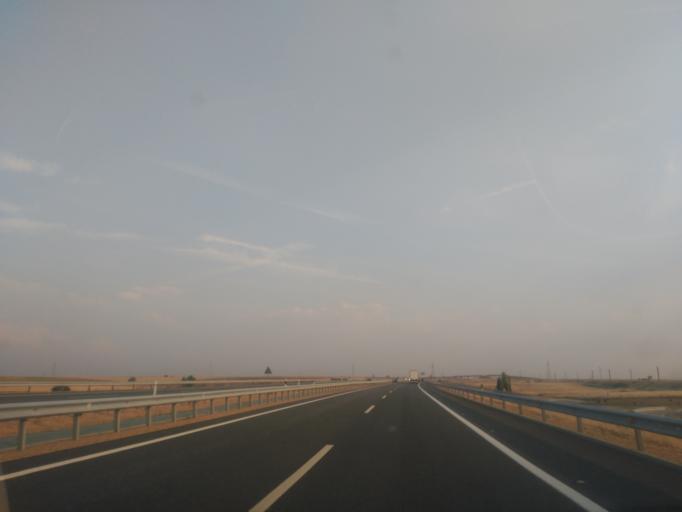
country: ES
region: Castille and Leon
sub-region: Provincia de Zamora
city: Montamarta
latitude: 41.6350
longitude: -5.7901
